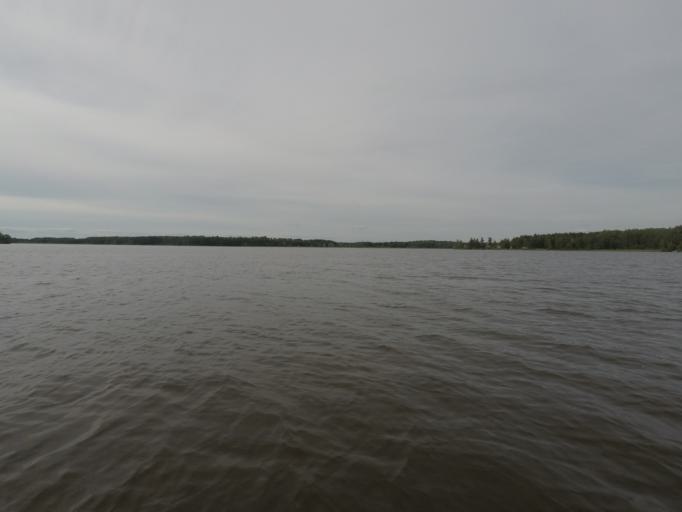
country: SE
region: Soedermanland
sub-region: Eskilstuna Kommun
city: Torshalla
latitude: 59.4829
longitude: 16.4156
